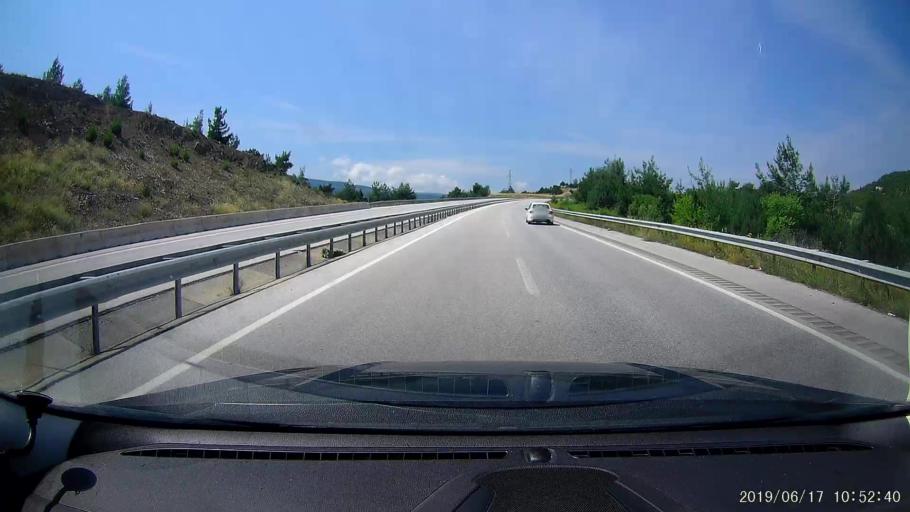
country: TR
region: Corum
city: Hacihamza
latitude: 41.0855
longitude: 34.3385
